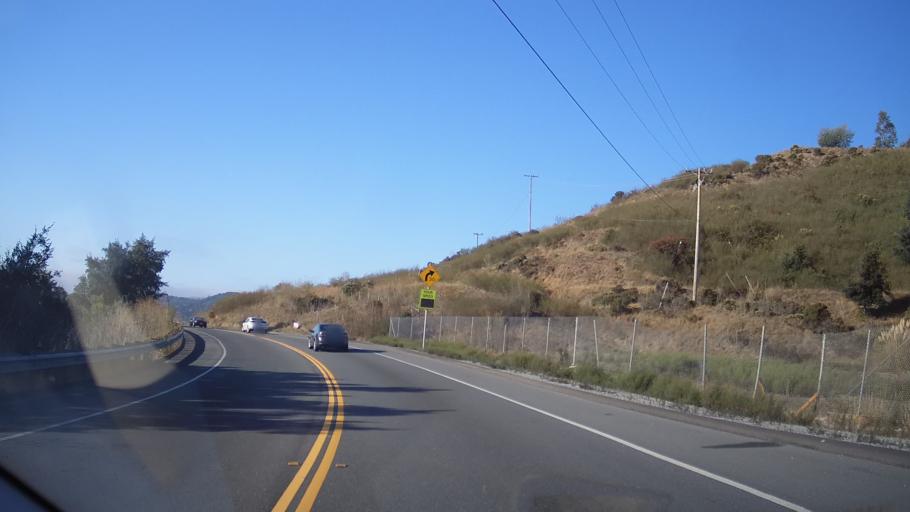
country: US
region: California
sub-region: Marin County
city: Corte Madera
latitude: 37.9443
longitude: -122.4972
